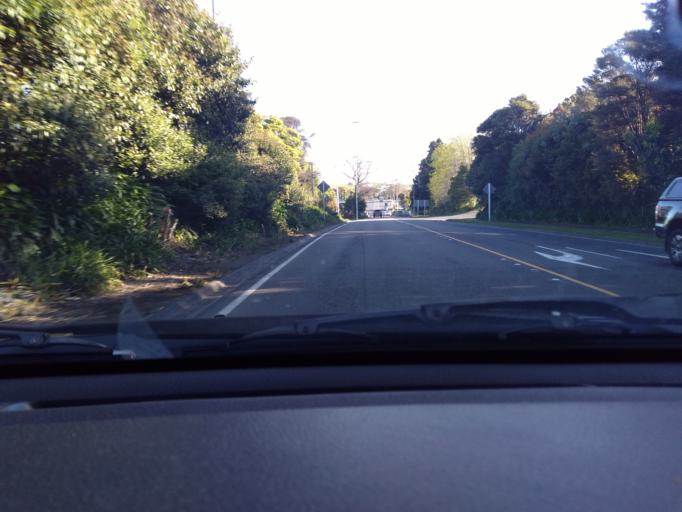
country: NZ
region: Auckland
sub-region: Auckland
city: Warkworth
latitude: -36.3983
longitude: 174.6607
